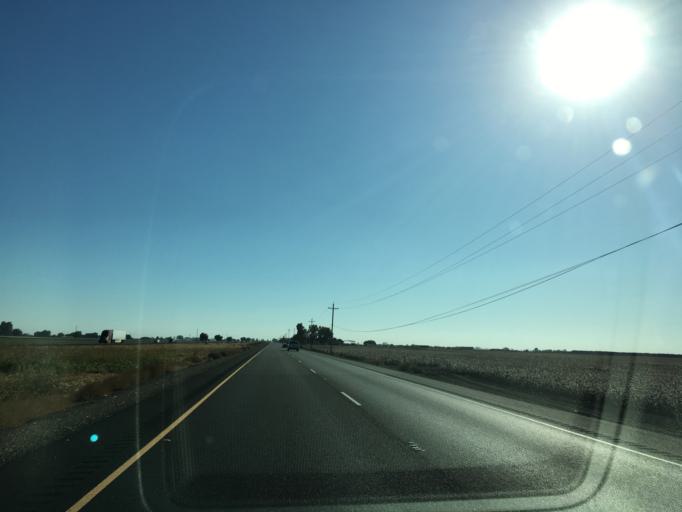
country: US
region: California
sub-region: Merced County
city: Dos Palos
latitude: 37.0475
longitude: -120.6159
